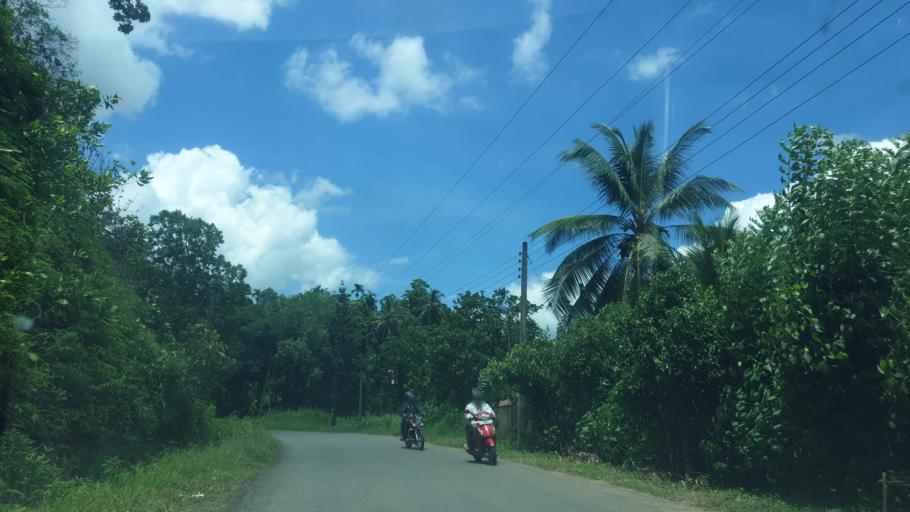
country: LK
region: Sabaragamuwa
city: Ratnapura
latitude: 6.4745
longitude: 80.4195
